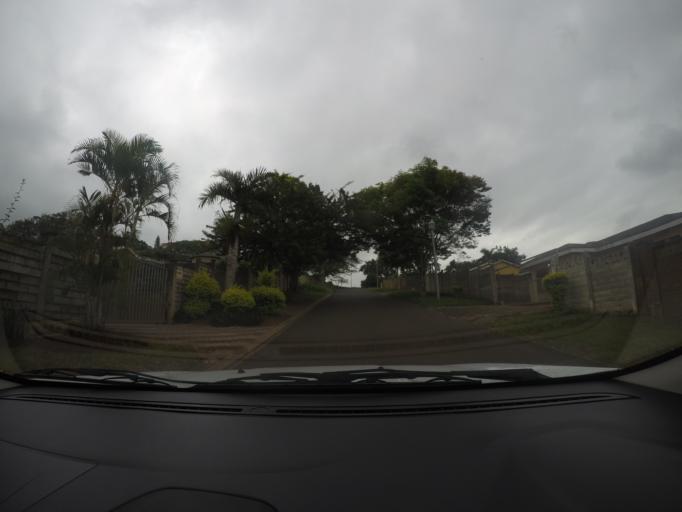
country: ZA
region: KwaZulu-Natal
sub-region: uThungulu District Municipality
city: Empangeni
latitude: -28.7610
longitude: 31.8831
